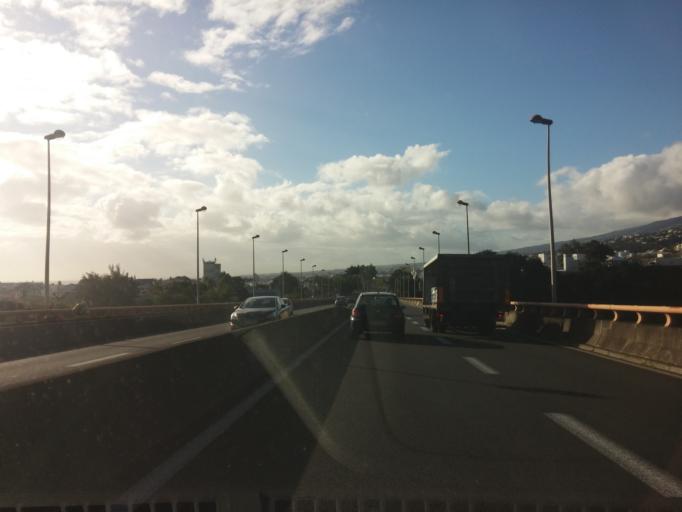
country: RE
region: Reunion
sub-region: Reunion
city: Saint-Denis
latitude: -20.8877
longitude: 55.4419
